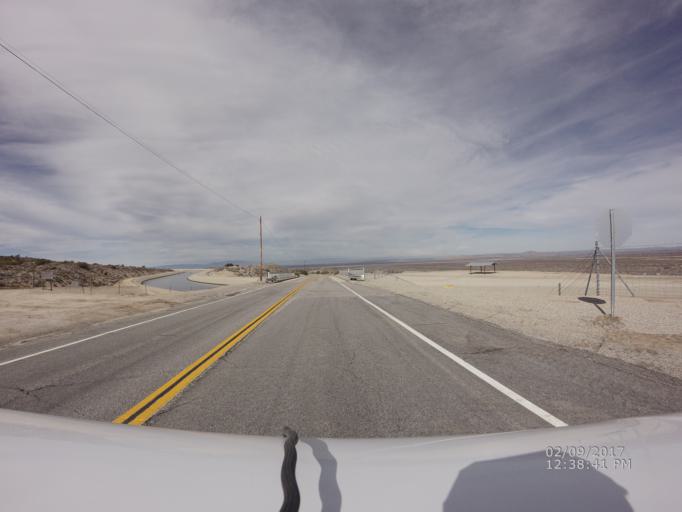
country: US
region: California
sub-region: Los Angeles County
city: Littlerock
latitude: 34.4766
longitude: -117.8619
